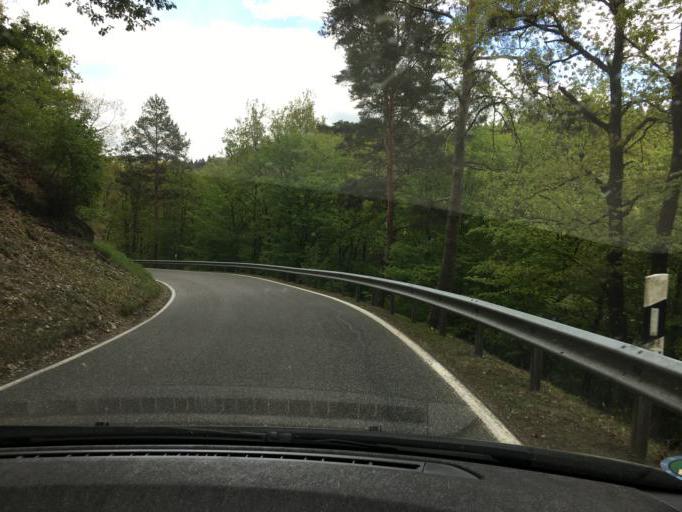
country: DE
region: Rheinland-Pfalz
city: Ahrbruck
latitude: 50.4895
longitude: 6.9587
